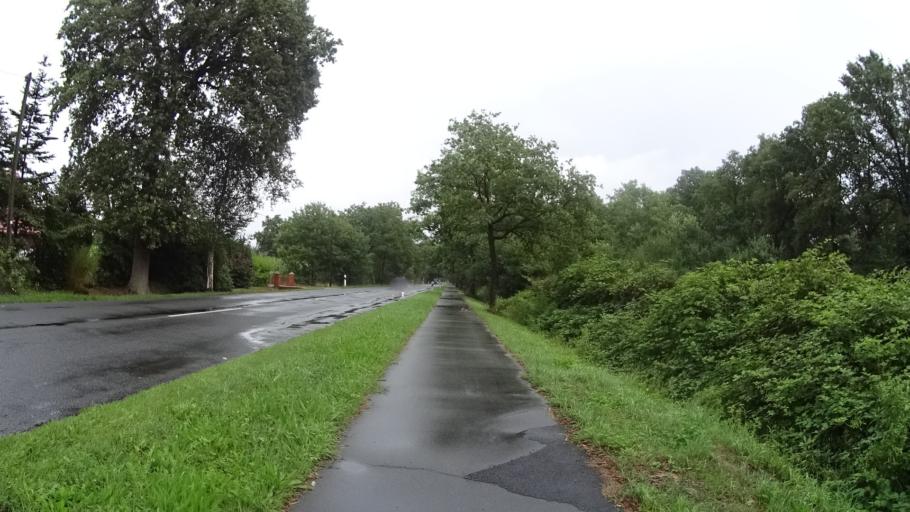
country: DE
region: Lower Saxony
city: Firrel
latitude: 53.3287
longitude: 7.6471
